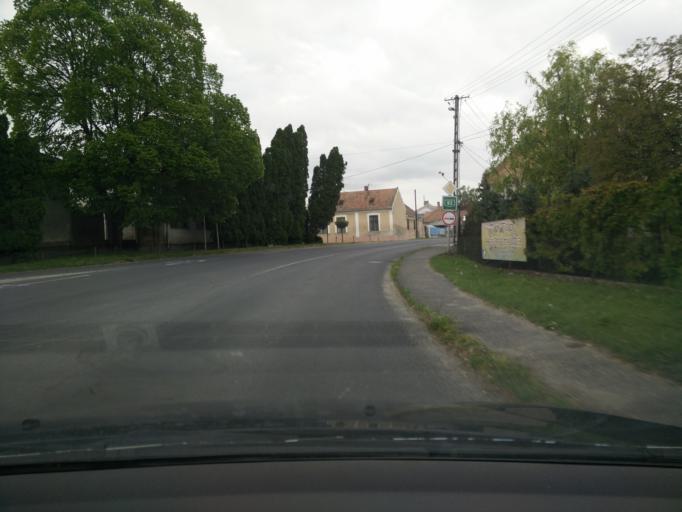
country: HU
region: Gyor-Moson-Sopron
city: Tet
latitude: 47.5139
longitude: 17.5155
